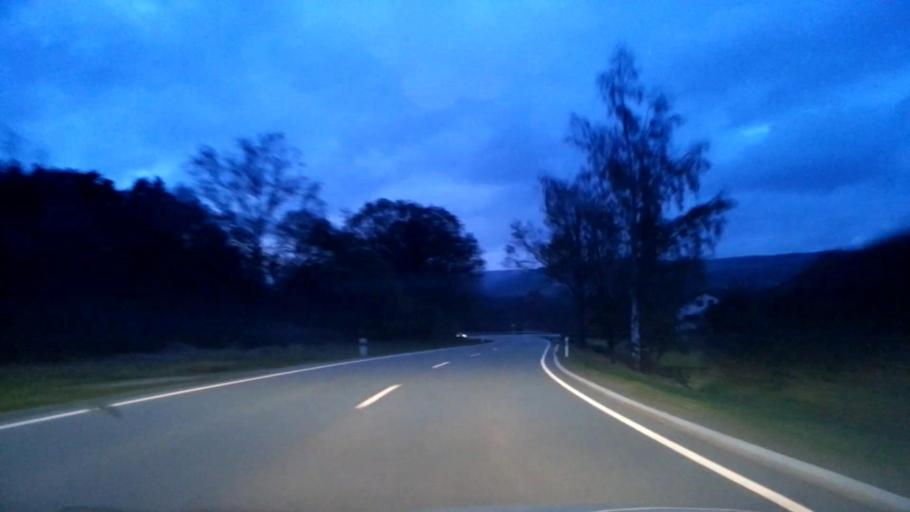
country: DE
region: Bavaria
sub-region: Upper Franconia
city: Kirchenpingarten
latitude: 49.9338
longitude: 11.7429
